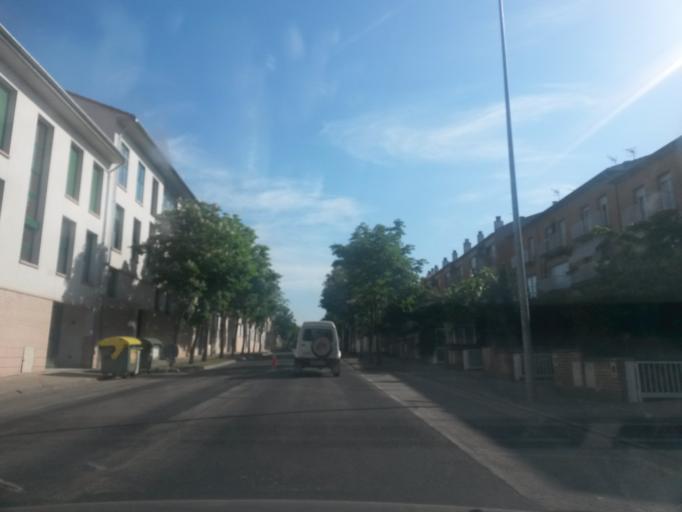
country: ES
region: Catalonia
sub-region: Provincia de Girona
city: Olot
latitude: 42.1781
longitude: 2.4940
